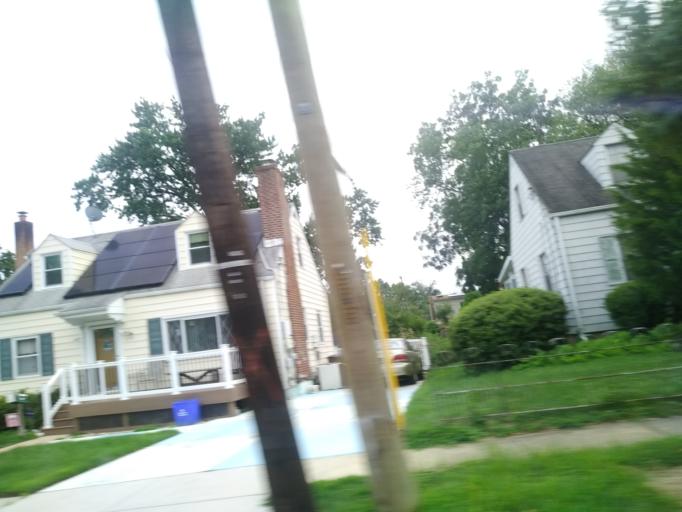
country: US
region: Maryland
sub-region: Montgomery County
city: Rockville
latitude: 39.0783
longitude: -77.1246
